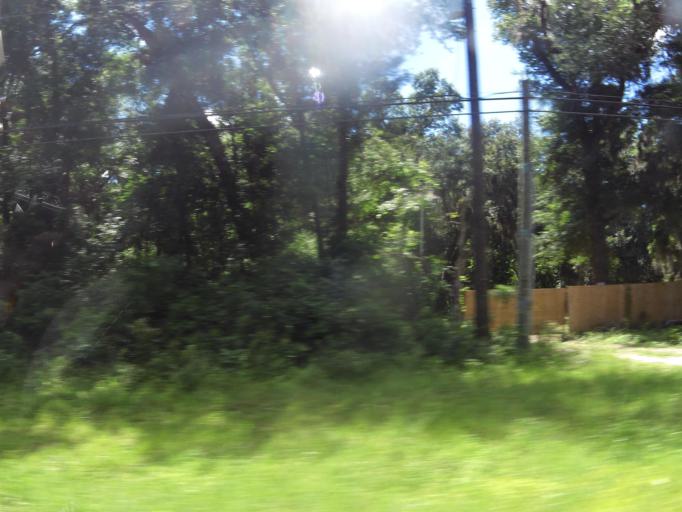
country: US
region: Florida
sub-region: Nassau County
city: Yulee
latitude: 30.6311
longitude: -81.5296
